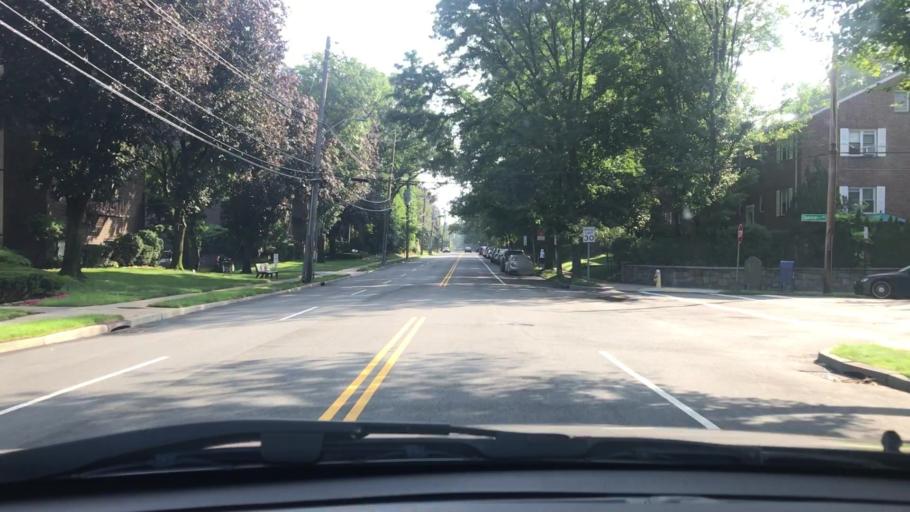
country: US
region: New York
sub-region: Westchester County
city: Larchmont
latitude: 40.9253
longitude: -73.7689
